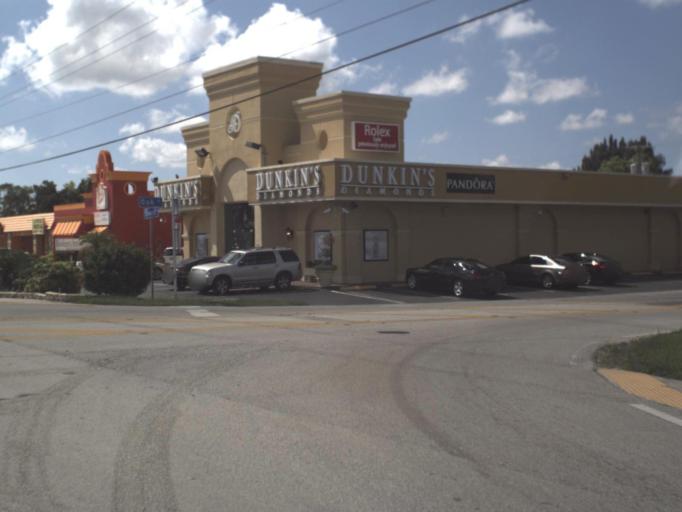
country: US
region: Florida
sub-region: Lee County
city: Pine Manor
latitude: 26.5730
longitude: -81.8721
